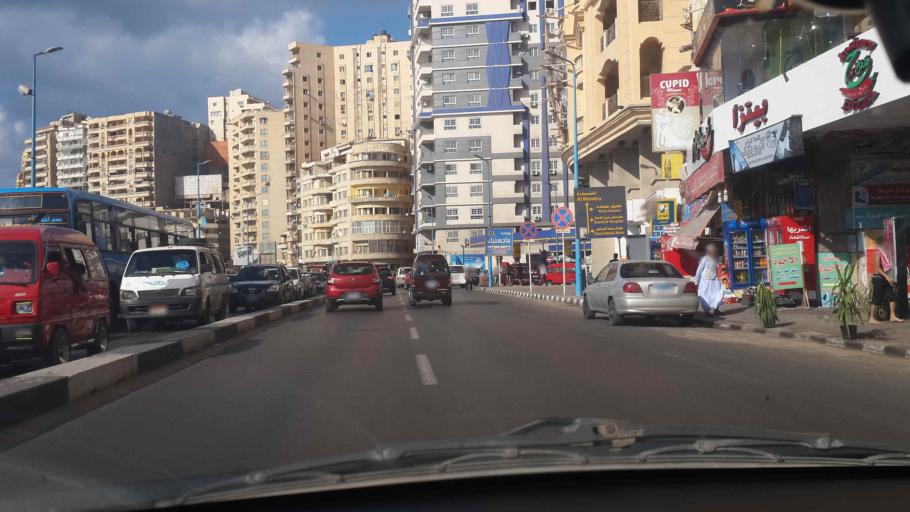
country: EG
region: Alexandria
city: Alexandria
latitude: 31.2651
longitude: 29.9871
